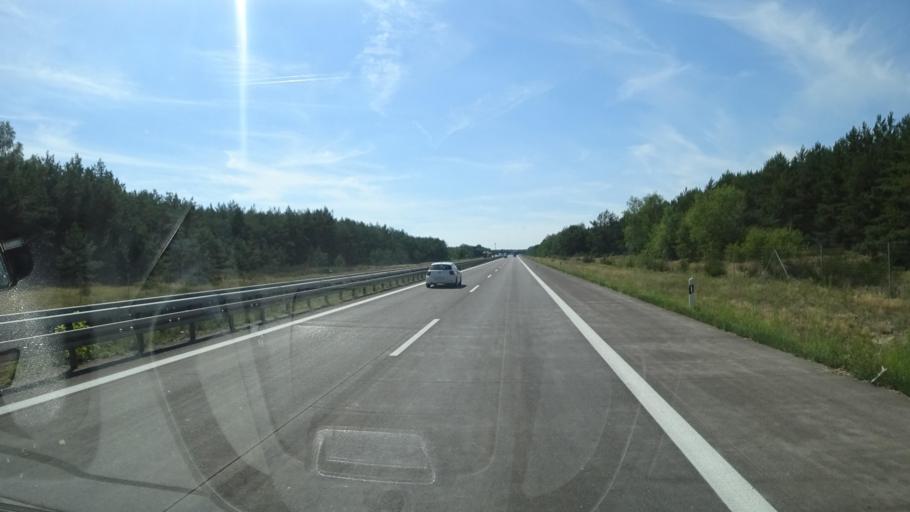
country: DE
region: Brandenburg
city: Spreenhagen
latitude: 52.3116
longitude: 13.8449
